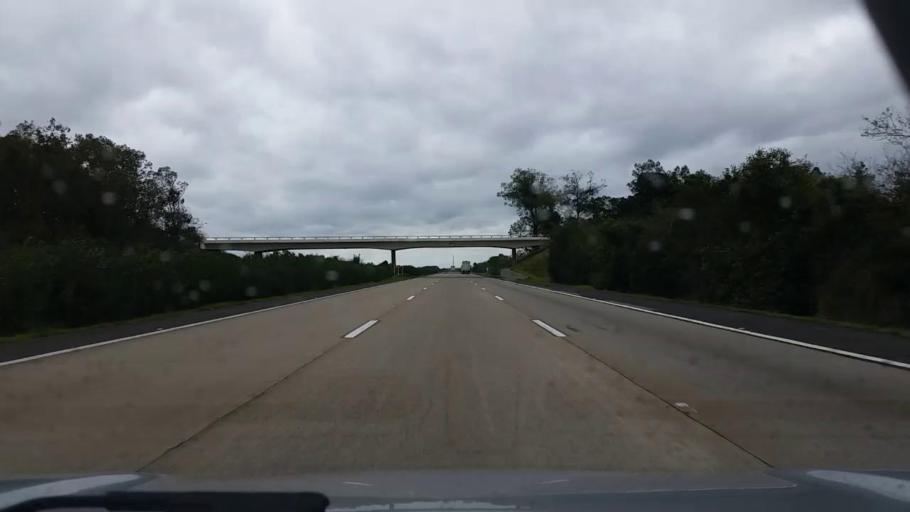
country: BR
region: Rio Grande do Sul
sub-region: Rolante
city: Rolante
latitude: -29.8862
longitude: -50.6529
